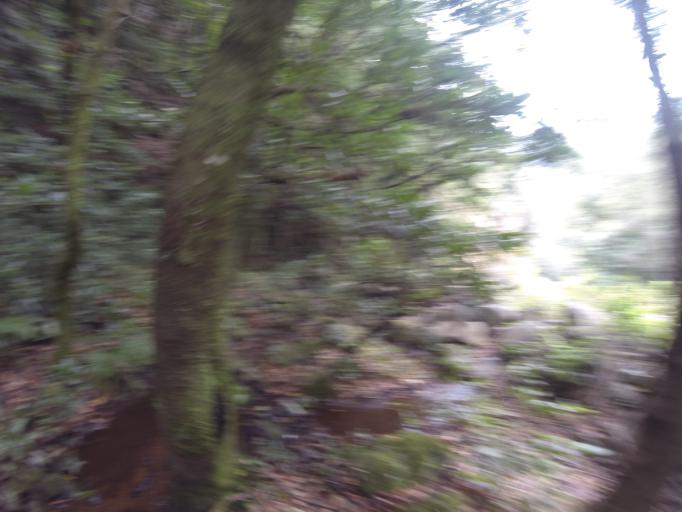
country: PT
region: Madeira
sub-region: Sao Vicente
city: Sao Vicente
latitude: 32.7913
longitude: -17.1143
